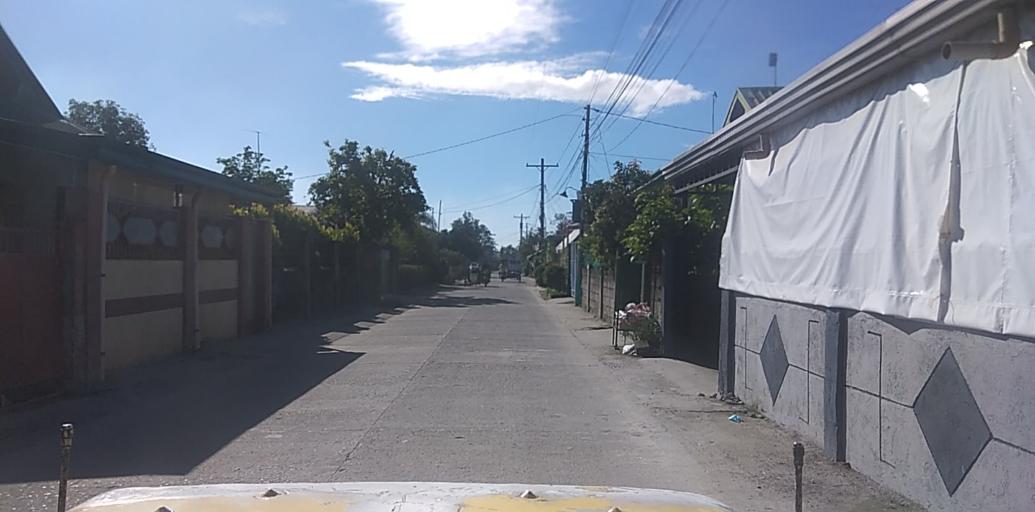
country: PH
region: Central Luzon
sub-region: Province of Pampanga
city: San Patricio
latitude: 15.1053
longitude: 120.7134
